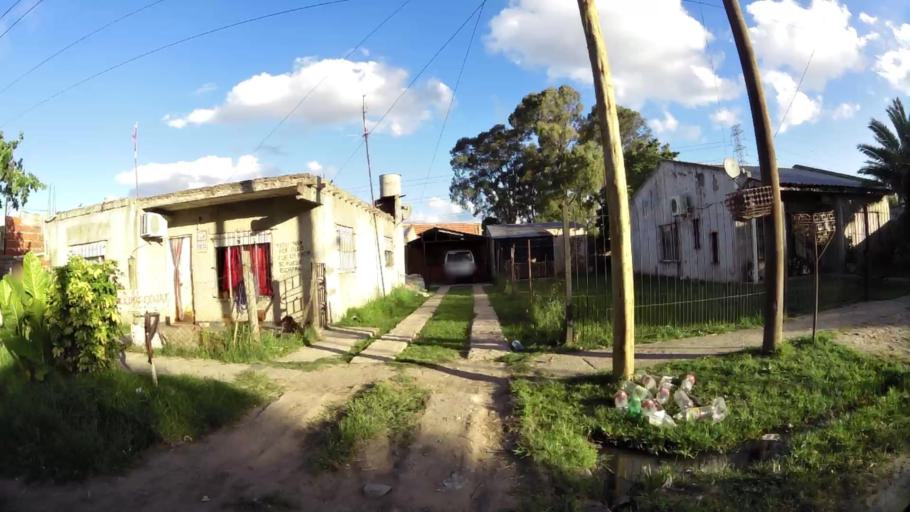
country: AR
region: Buenos Aires
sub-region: Partido de Moron
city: Moron
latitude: -34.7098
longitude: -58.6180
